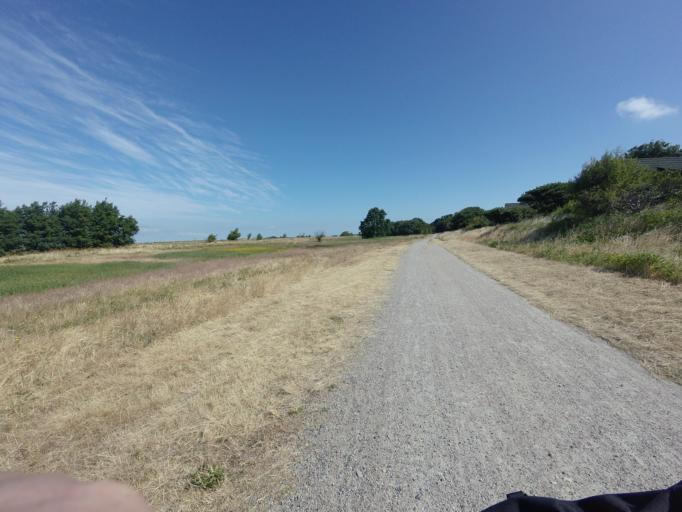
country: SE
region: Skane
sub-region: Vellinge Kommun
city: Skanor med Falsterbo
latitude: 55.4022
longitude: 12.8344
